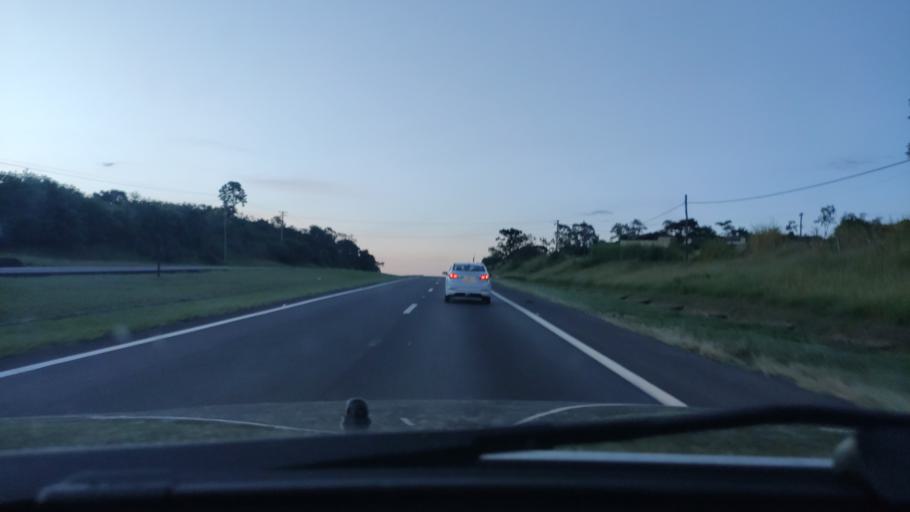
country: BR
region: Sao Paulo
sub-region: Sao Carlos
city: Sao Carlos
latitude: -22.0851
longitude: -47.8359
